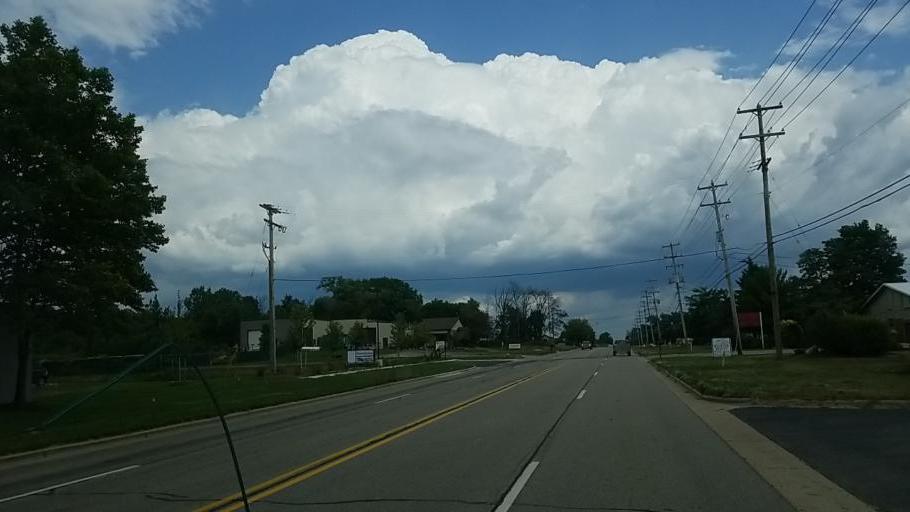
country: US
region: Michigan
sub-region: Kent County
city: Walker
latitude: 43.0157
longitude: -85.7569
